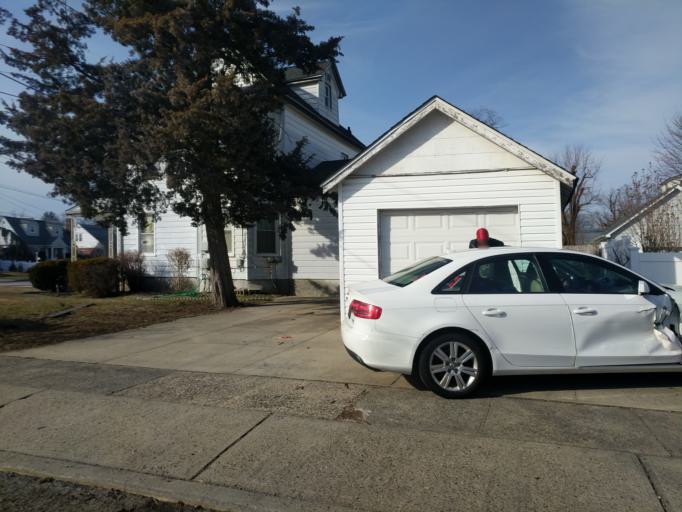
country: US
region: New York
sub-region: Nassau County
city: South Valley Stream
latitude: 40.6676
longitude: -73.7262
